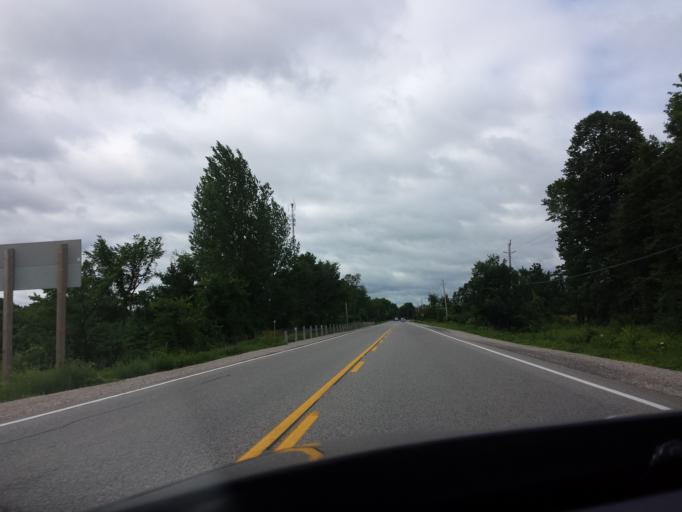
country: CA
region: Ontario
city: Carleton Place
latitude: 45.1133
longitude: -76.2177
